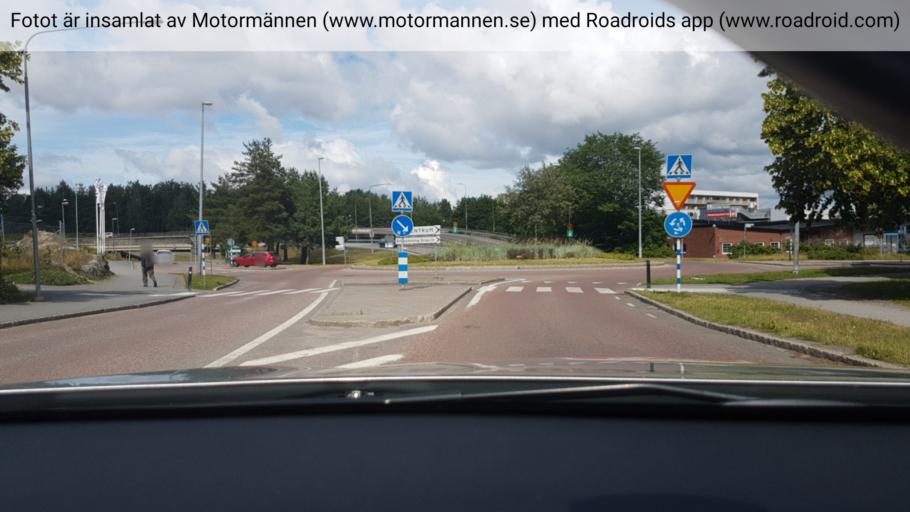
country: SE
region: Stockholm
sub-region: Tyreso Kommun
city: Bollmora
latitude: 59.2469
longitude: 18.2163
